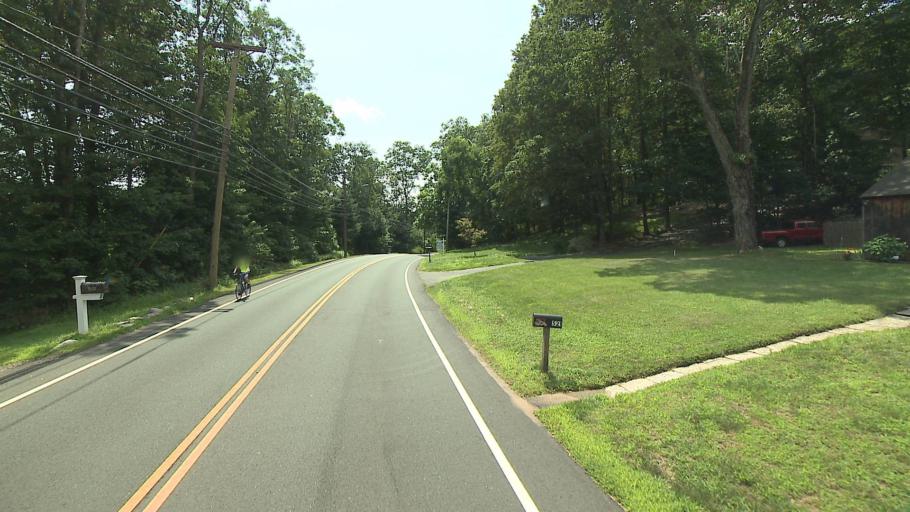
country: US
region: Connecticut
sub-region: Hartford County
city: Collinsville
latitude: 41.7804
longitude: -72.8910
